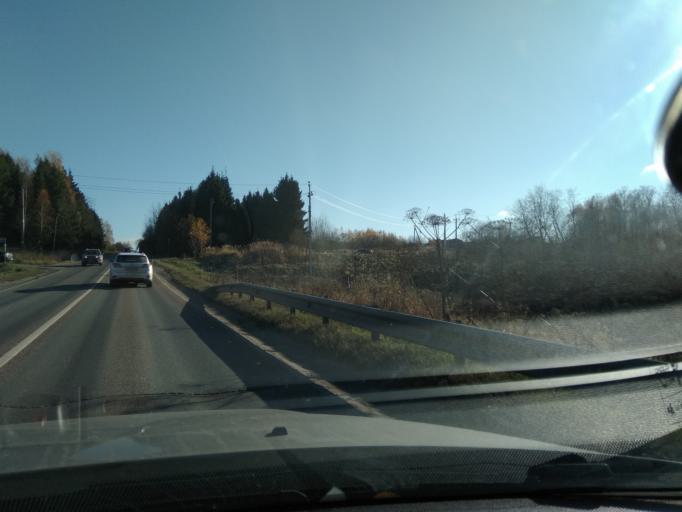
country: RU
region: Moskovskaya
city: Istra
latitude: 55.9319
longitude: 36.9256
